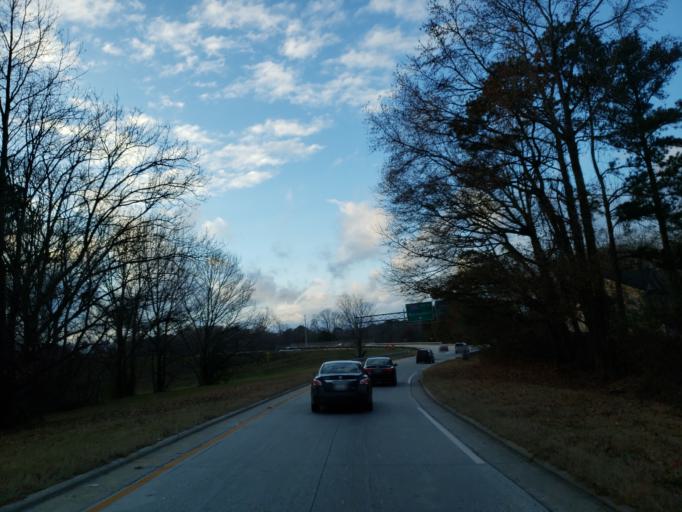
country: US
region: Georgia
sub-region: Fulton County
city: East Point
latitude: 33.6906
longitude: -84.4974
